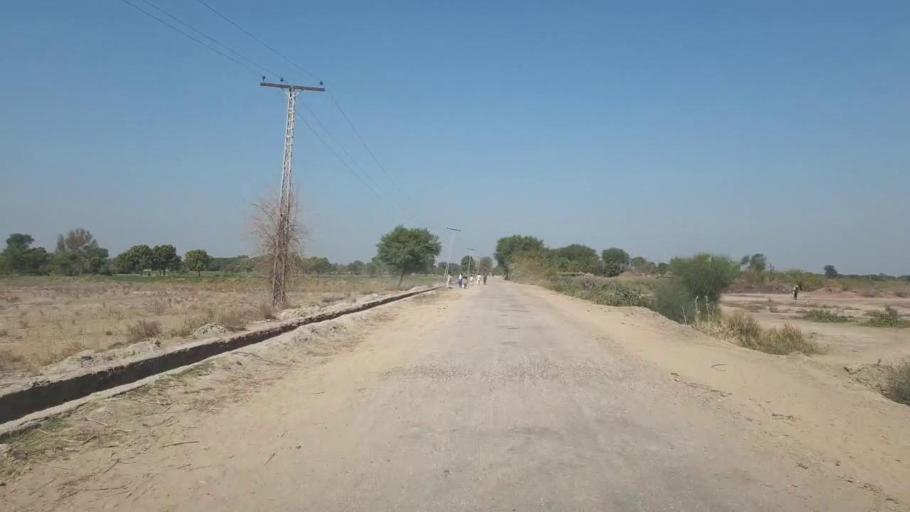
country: PK
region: Sindh
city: Chambar
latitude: 25.2942
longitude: 68.6918
